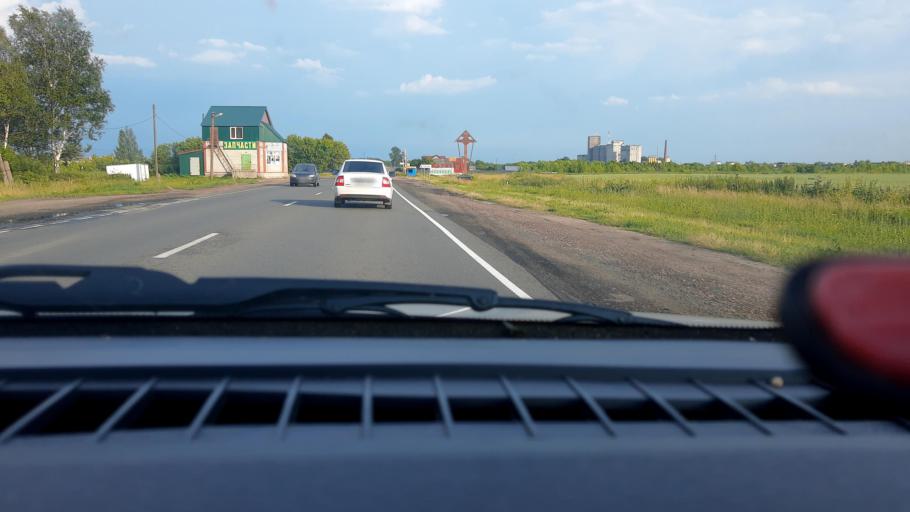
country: RU
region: Nizjnij Novgorod
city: Shatki
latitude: 55.2061
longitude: 44.0944
